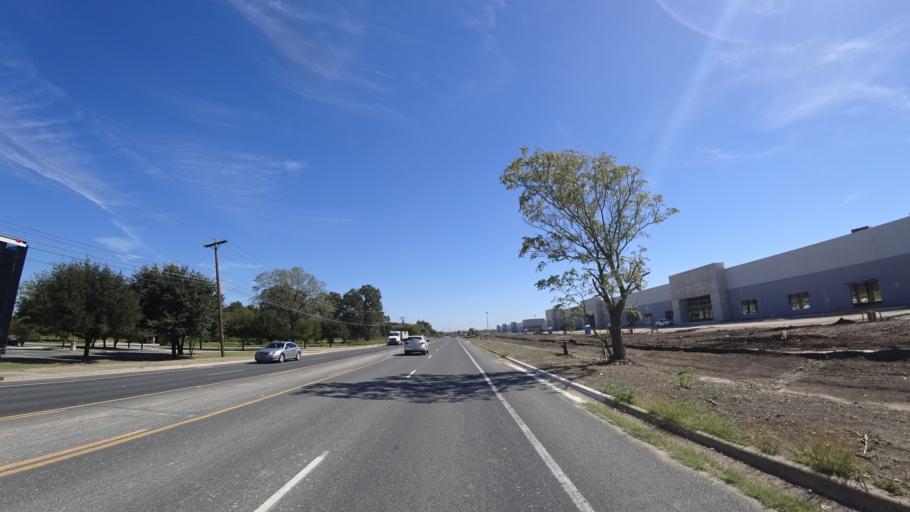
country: US
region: Texas
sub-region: Travis County
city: Austin
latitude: 30.1869
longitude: -97.6929
